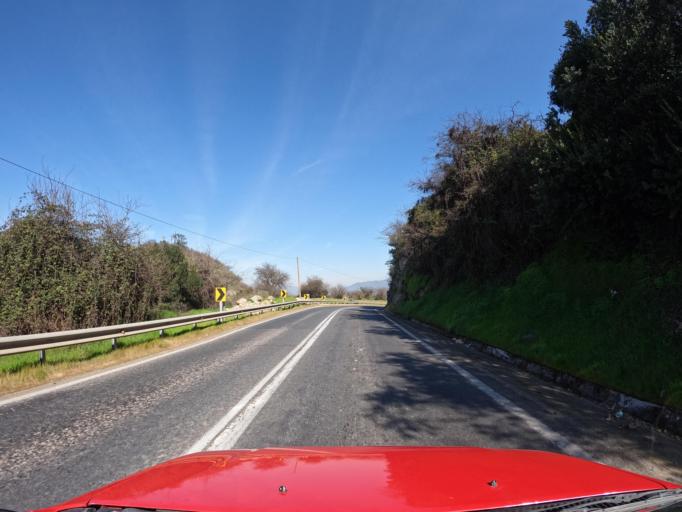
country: CL
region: Maule
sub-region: Provincia de Curico
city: Rauco
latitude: -34.9777
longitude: -71.3877
